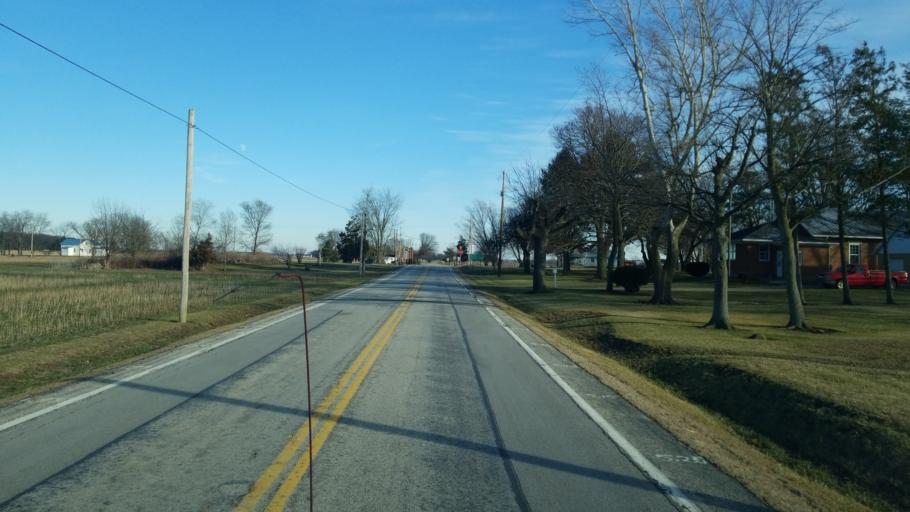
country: US
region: Ohio
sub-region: Huron County
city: Bellevue
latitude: 41.2023
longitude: -82.8259
